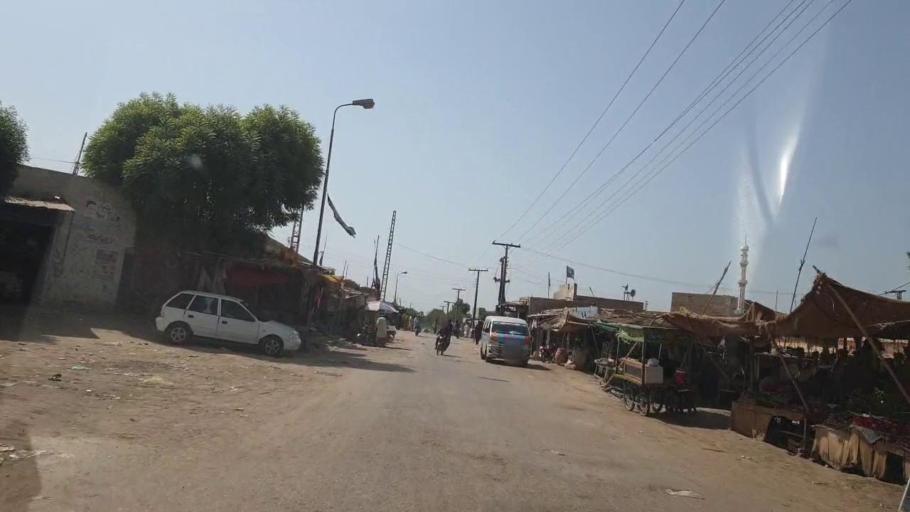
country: PK
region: Sindh
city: Setharja Old
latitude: 27.1307
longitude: 68.5341
